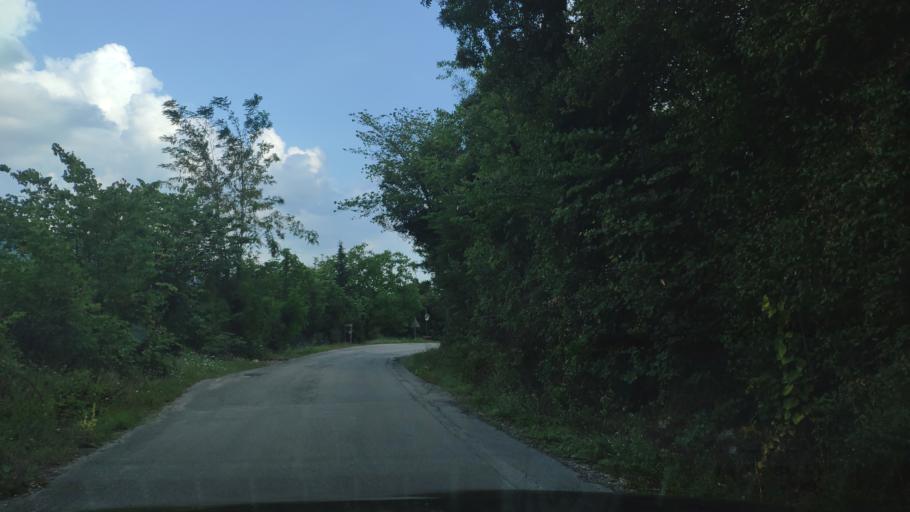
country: GR
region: Epirus
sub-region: Nomos Artas
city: Agios Dimitrios
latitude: 39.4432
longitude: 21.0153
